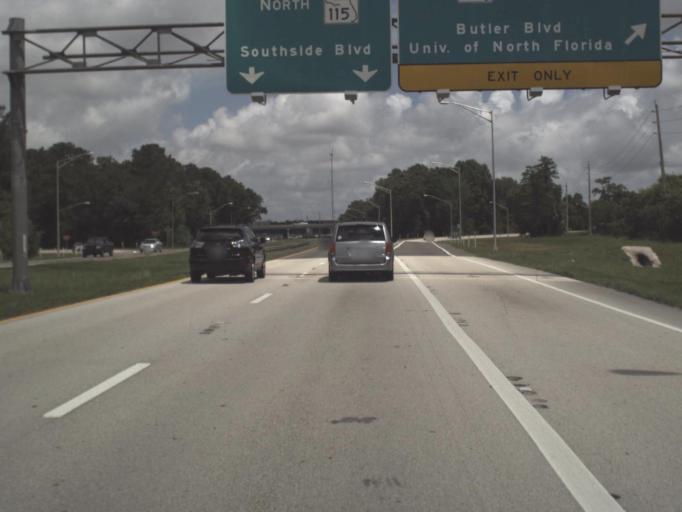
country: US
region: Florida
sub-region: Duval County
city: Jacksonville
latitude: 30.2451
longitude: -81.5520
